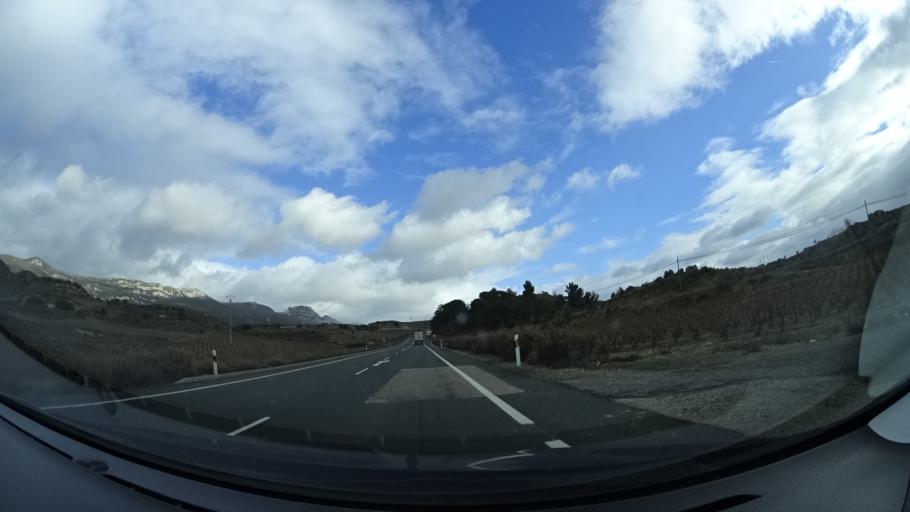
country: ES
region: La Rioja
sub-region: Provincia de La Rioja
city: Abalos
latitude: 42.5690
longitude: -2.7234
